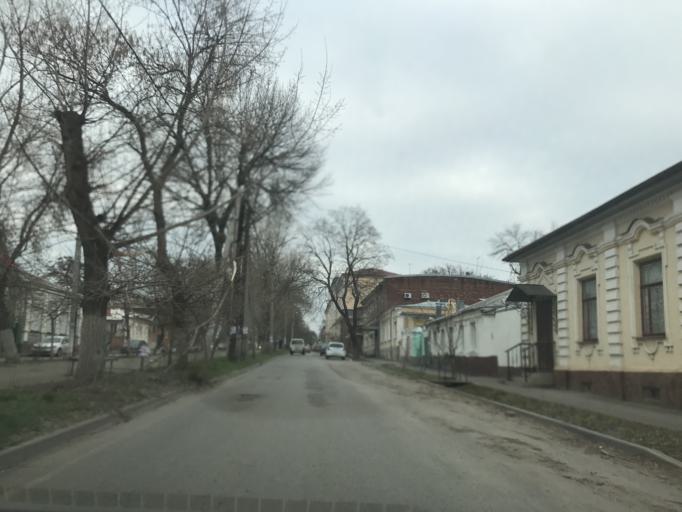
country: RU
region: Rostov
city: Novocherkassk
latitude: 47.4123
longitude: 40.0953
